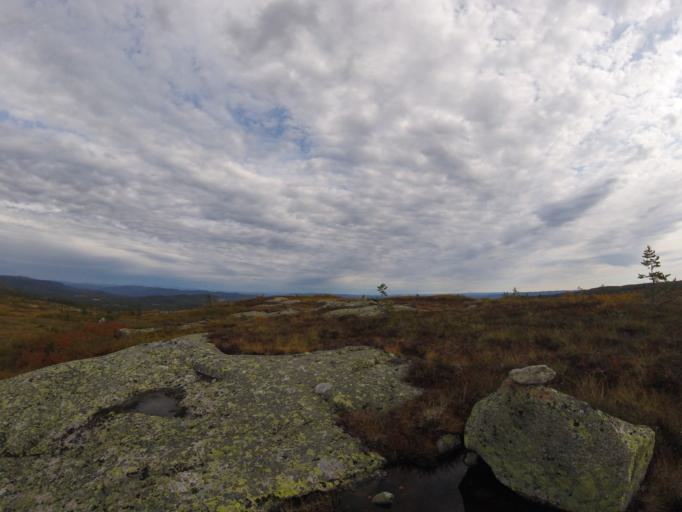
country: NO
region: Buskerud
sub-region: Rollag
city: Rollag
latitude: 59.8080
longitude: 9.3156
